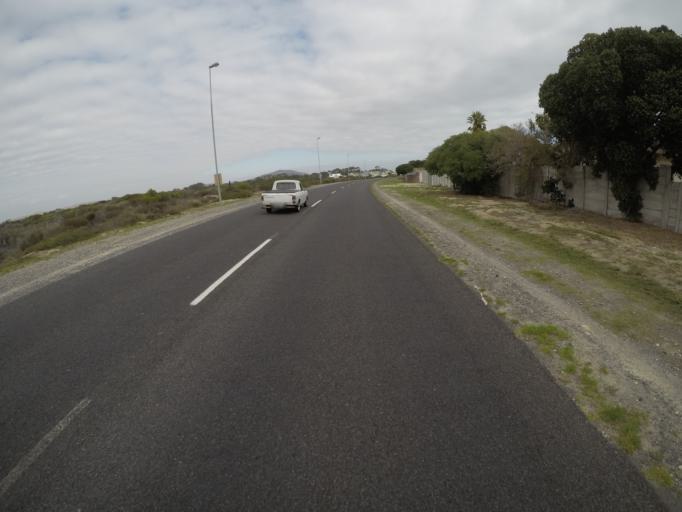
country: ZA
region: Western Cape
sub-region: City of Cape Town
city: Atlantis
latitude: -33.7078
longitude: 18.4471
